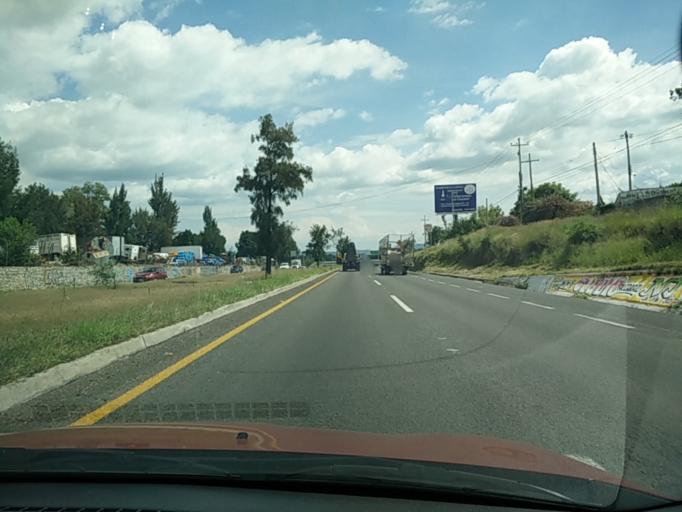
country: MX
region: Jalisco
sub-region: Tlajomulco de Zuniga
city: Rancho Alegre [Fraccionamiento]
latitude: 20.4727
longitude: -103.2622
